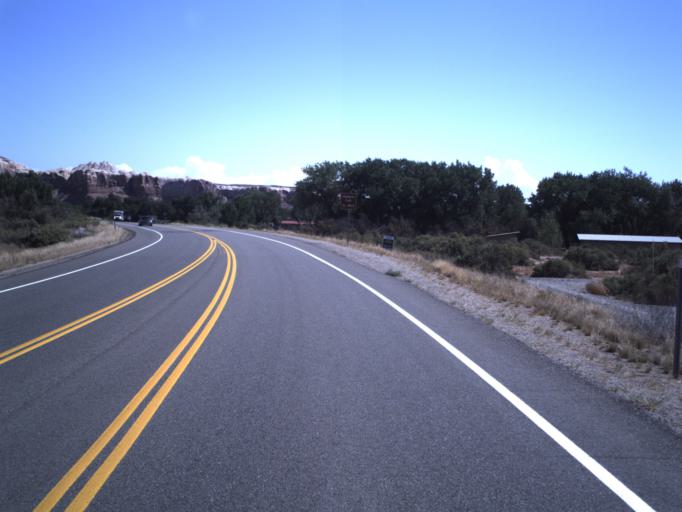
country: US
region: Utah
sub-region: San Juan County
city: Blanding
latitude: 37.2818
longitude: -109.5635
